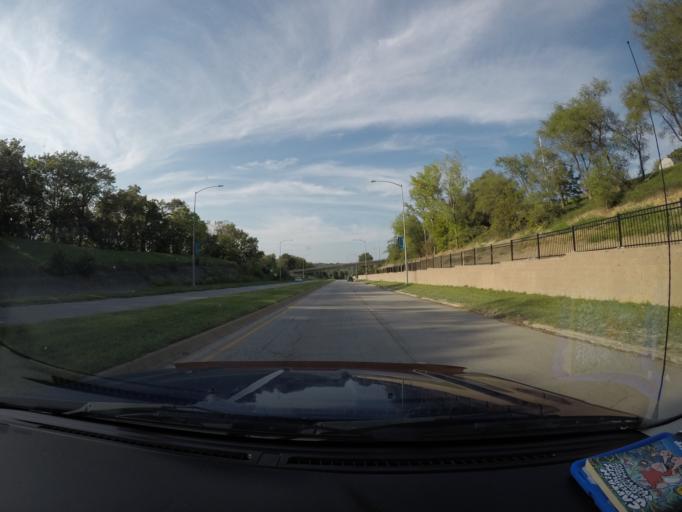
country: US
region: Kansas
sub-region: Atchison County
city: Atchison
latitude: 39.5499
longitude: -95.1293
